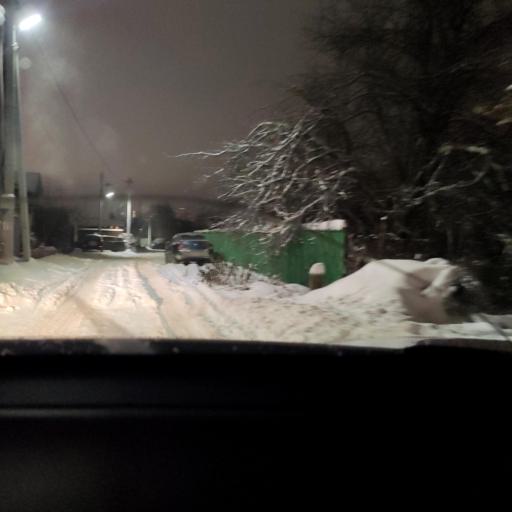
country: RU
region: Tatarstan
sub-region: Gorod Kazan'
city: Kazan
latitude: 55.7248
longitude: 49.1343
